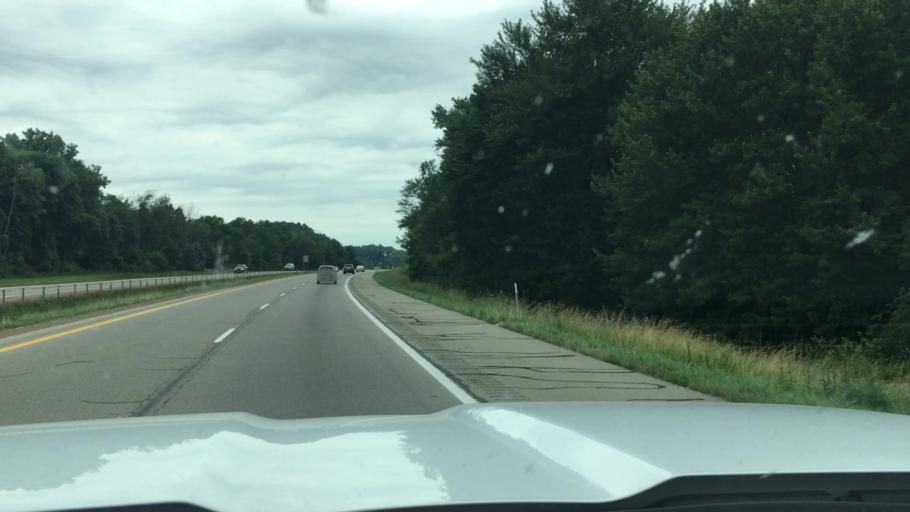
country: US
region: Michigan
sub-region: Allegan County
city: Wayland
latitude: 42.6059
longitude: -85.6601
